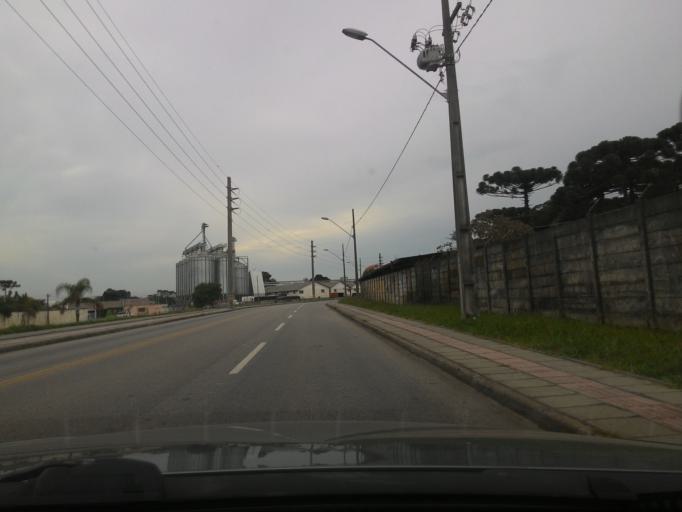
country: BR
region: Parana
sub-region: Pinhais
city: Pinhais
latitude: -25.4448
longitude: -49.1863
